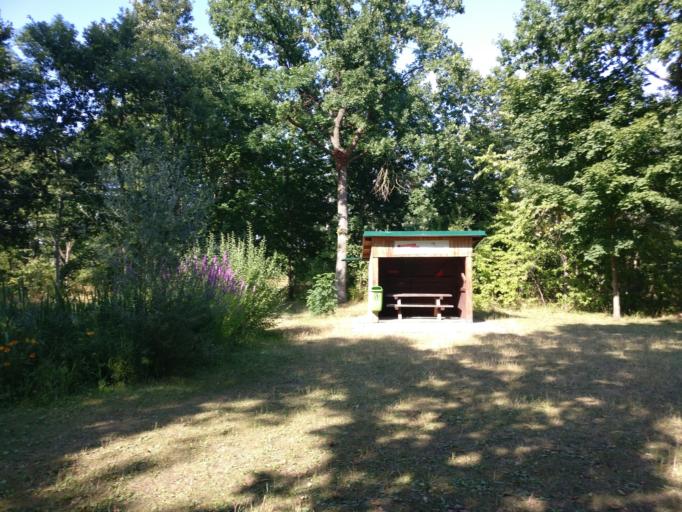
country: AT
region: Lower Austria
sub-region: Politischer Bezirk Ganserndorf
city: Strasshof an der Nordbahn
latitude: 48.3020
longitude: 16.6443
